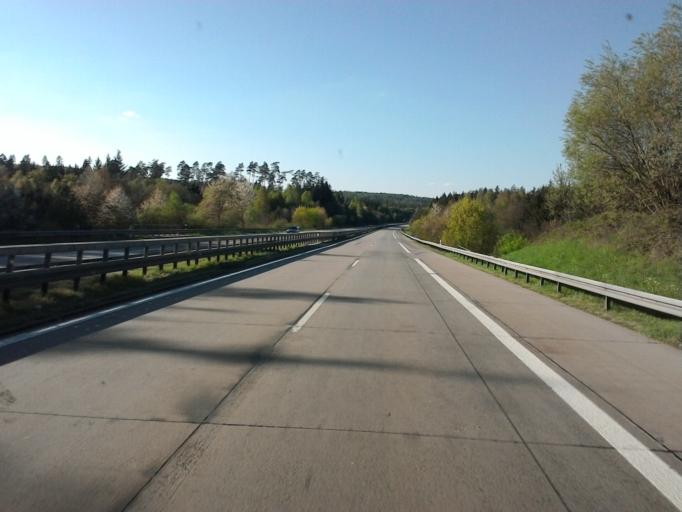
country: DE
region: Baden-Wuerttemberg
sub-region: Regierungsbezirk Stuttgart
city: Ellenberg
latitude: 48.9943
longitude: 10.1948
